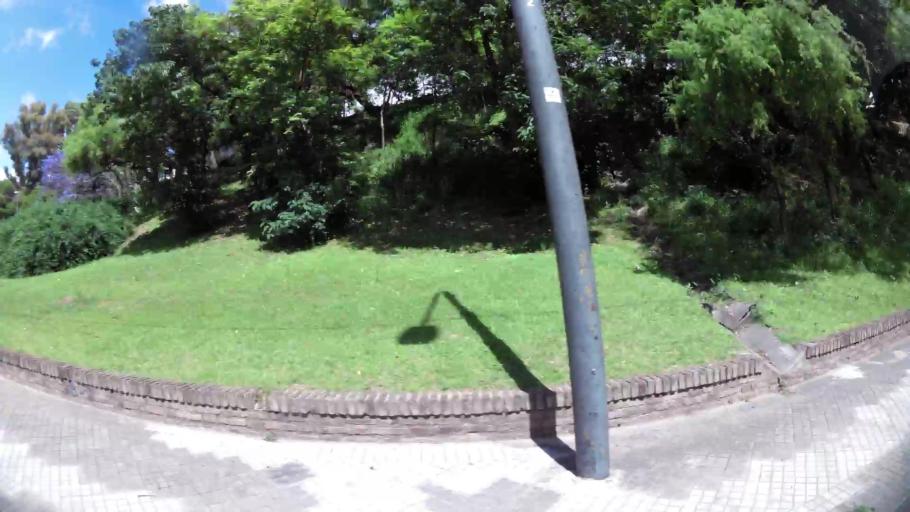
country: AR
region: Santa Fe
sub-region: Departamento de Rosario
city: Rosario
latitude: -32.9601
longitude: -60.6213
